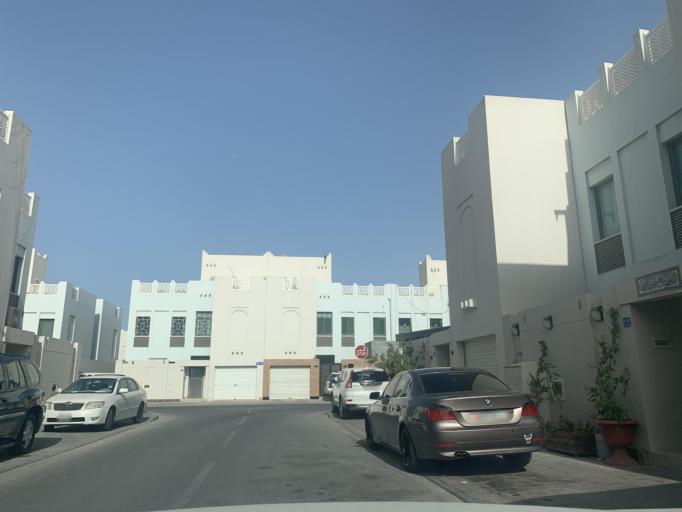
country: BH
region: Northern
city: Sitrah
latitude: 26.1593
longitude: 50.6272
